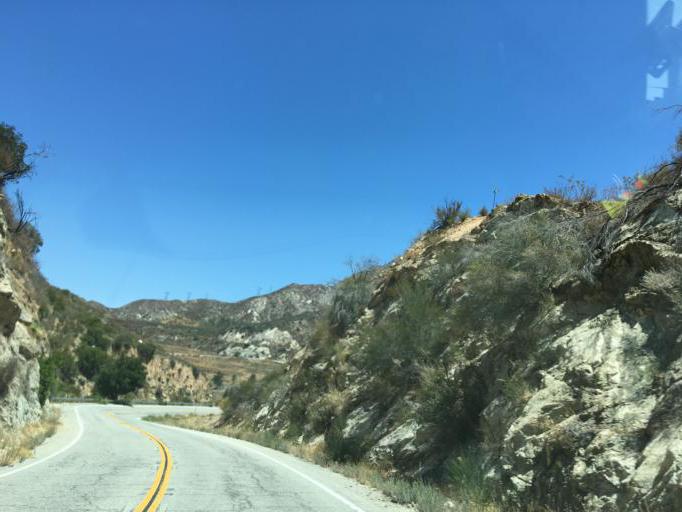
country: US
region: California
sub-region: Los Angeles County
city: La Crescenta-Montrose
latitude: 34.2835
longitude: -118.1998
